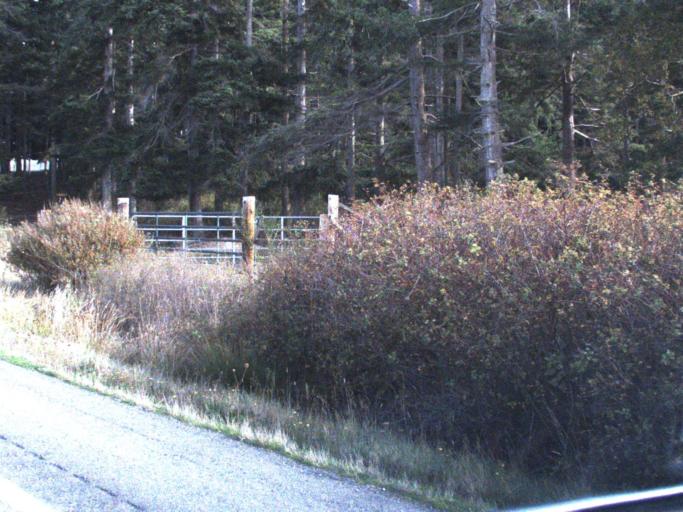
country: US
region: Washington
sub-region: Island County
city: Coupeville
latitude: 48.2625
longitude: -122.6899
